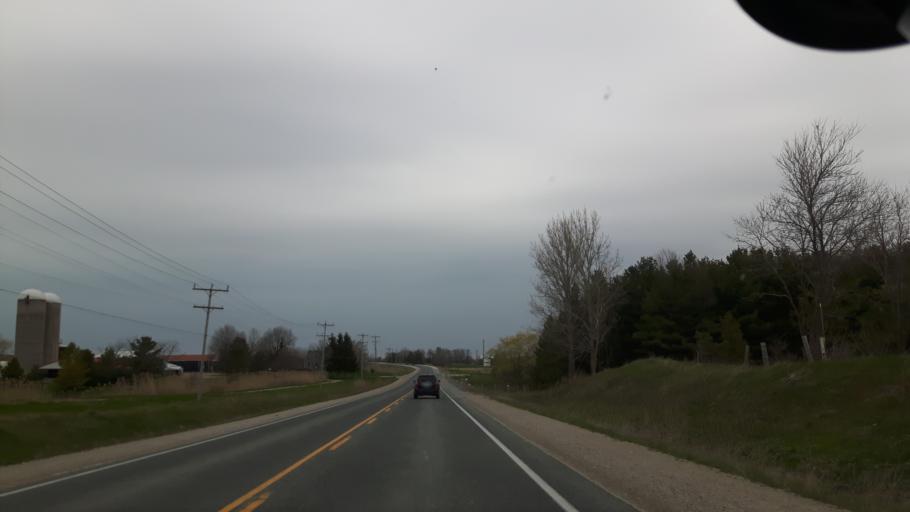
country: CA
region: Ontario
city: Goderich
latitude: 43.6856
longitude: -81.6308
